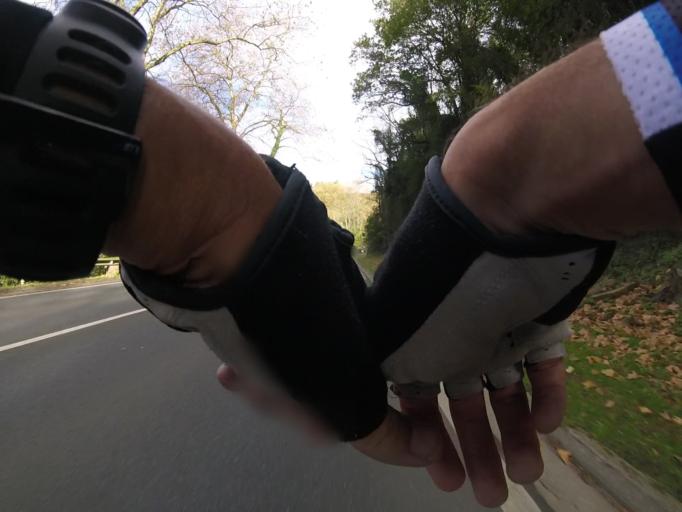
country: ES
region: Basque Country
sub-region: Provincia de Guipuzcoa
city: Usurbil
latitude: 43.2756
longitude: -2.0561
